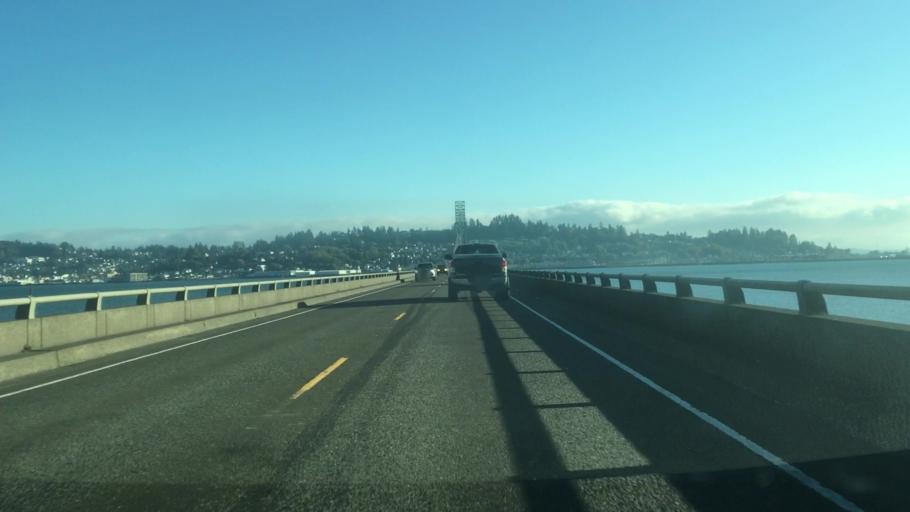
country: US
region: Oregon
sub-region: Clatsop County
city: Astoria
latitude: 46.2066
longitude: -123.8576
